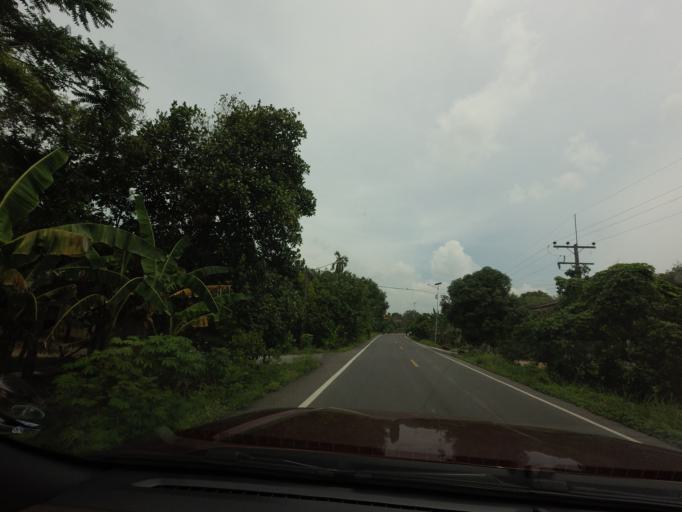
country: TH
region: Pattani
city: Yarang
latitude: 6.7132
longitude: 101.2941
